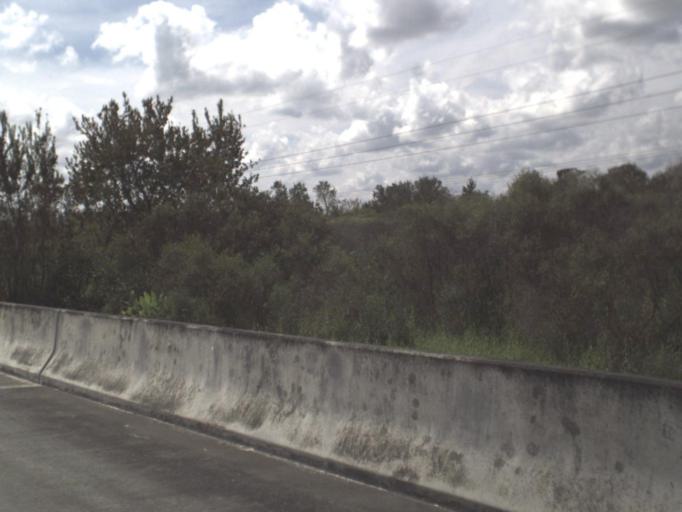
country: US
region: Florida
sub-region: Collier County
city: Immokalee
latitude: 26.2129
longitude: -81.3456
